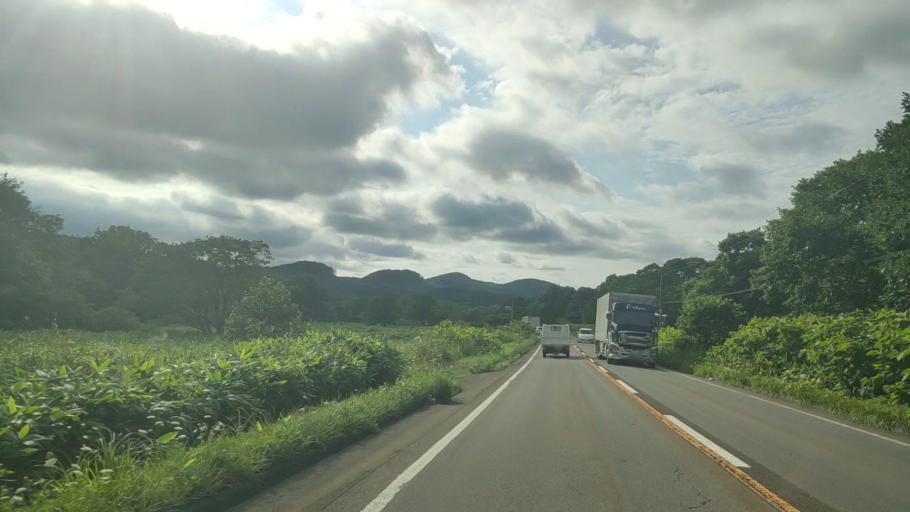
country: JP
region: Hokkaido
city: Niseko Town
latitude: 42.6003
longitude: 140.4953
